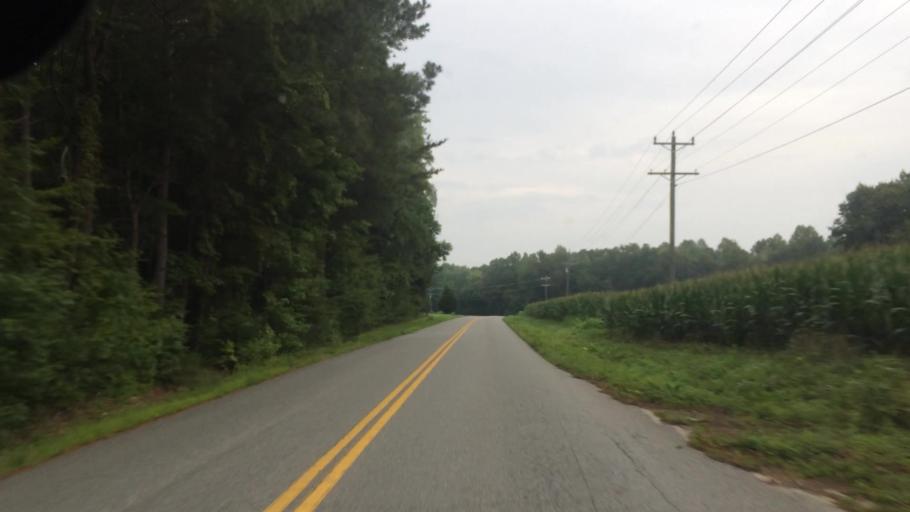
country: US
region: Virginia
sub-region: King William County
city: West Point
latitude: 37.5577
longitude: -76.7073
